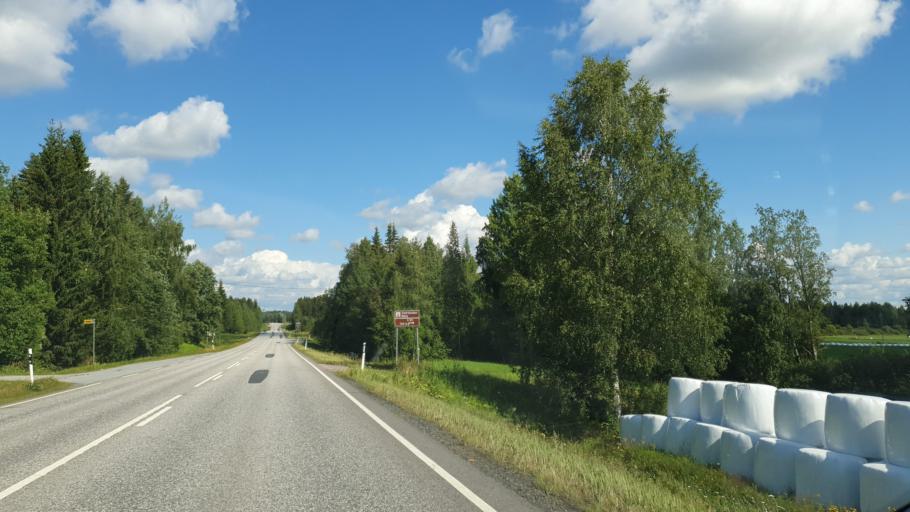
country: FI
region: Northern Savo
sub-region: Ylae-Savo
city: Sonkajaervi
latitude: 63.7194
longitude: 27.3671
